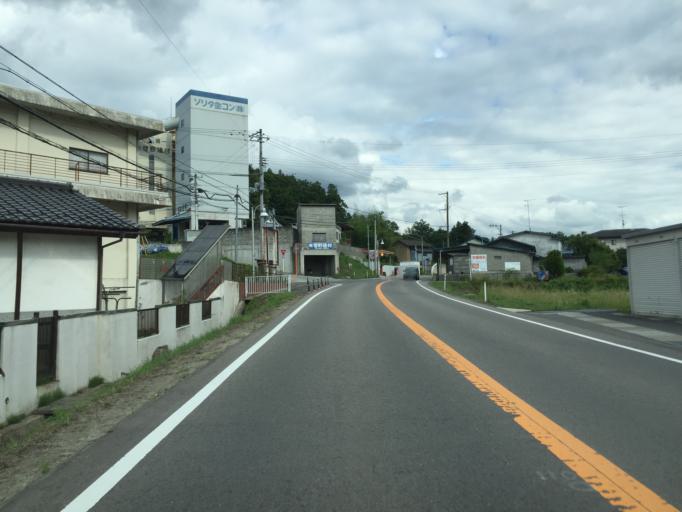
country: JP
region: Fukushima
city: Fukushima-shi
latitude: 37.6685
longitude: 140.5289
